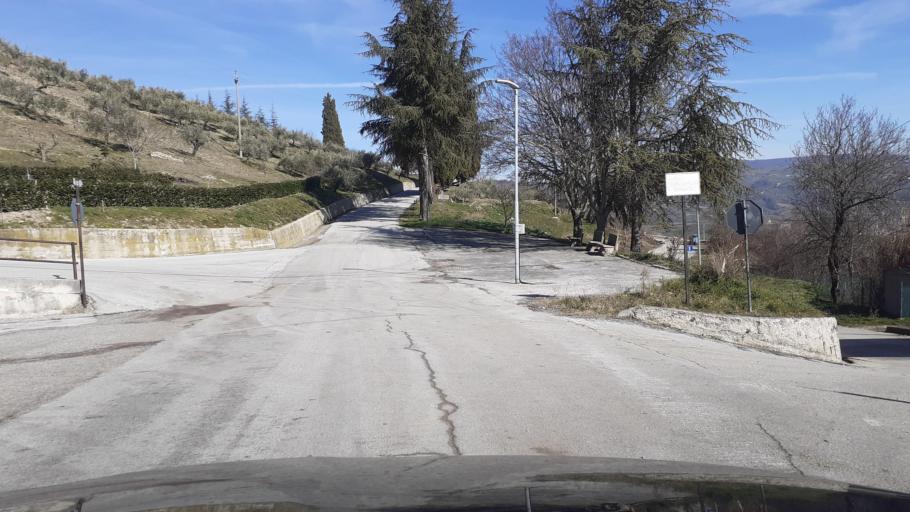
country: IT
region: Molise
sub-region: Provincia di Campobasso
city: Pietracupa
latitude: 41.6831
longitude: 14.5220
